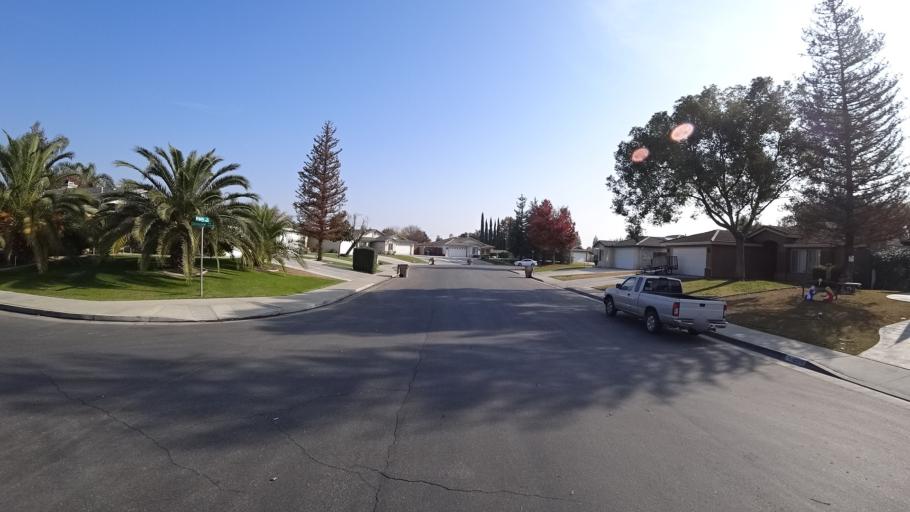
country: US
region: California
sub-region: Kern County
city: Greenacres
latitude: 35.4077
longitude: -119.1171
